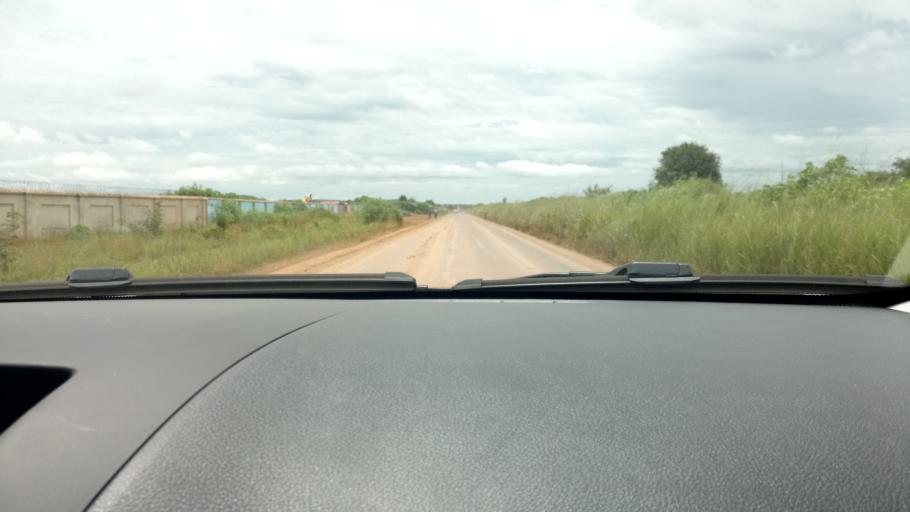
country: CD
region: Katanga
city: Lubumbashi
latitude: -11.5732
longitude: 27.5404
